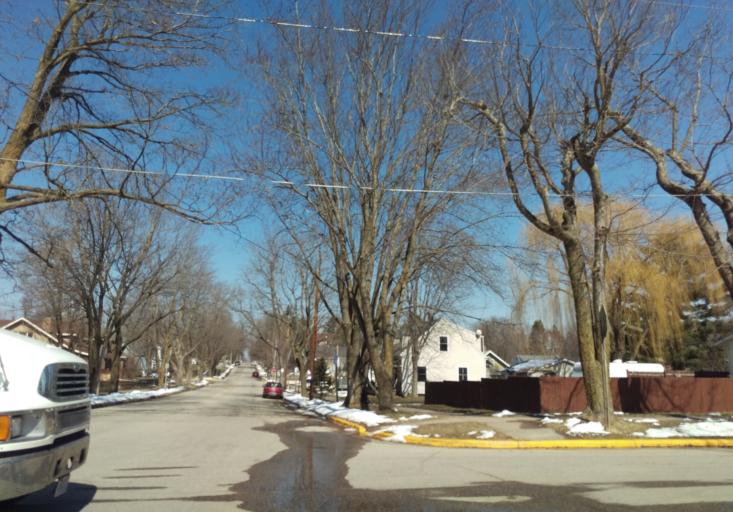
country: US
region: Wisconsin
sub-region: Vernon County
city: Viroqua
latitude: 43.5509
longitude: -90.8867
